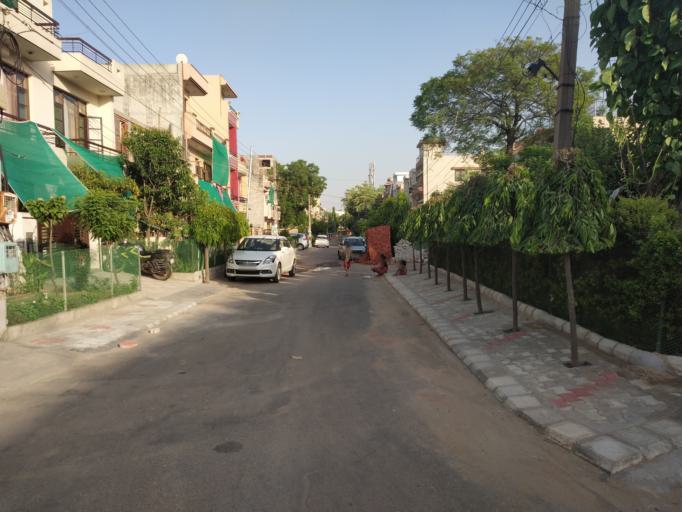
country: IN
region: Punjab
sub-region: Ajitgarh
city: Mohali
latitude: 30.6862
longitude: 76.7480
